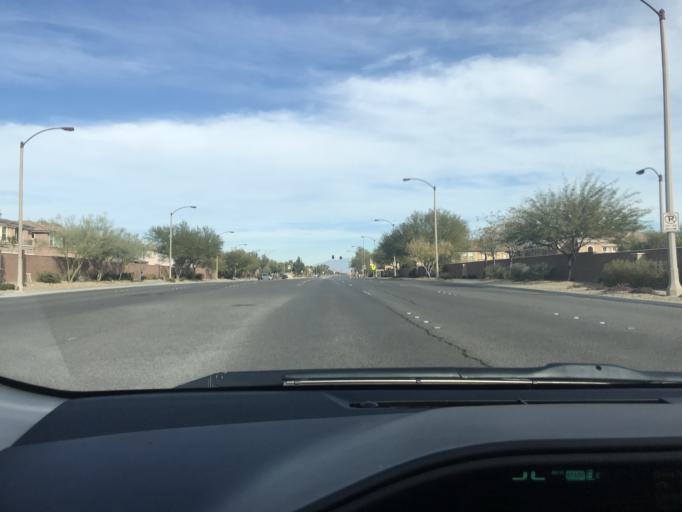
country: US
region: Nevada
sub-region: Clark County
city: Enterprise
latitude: 36.0101
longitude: -115.2799
